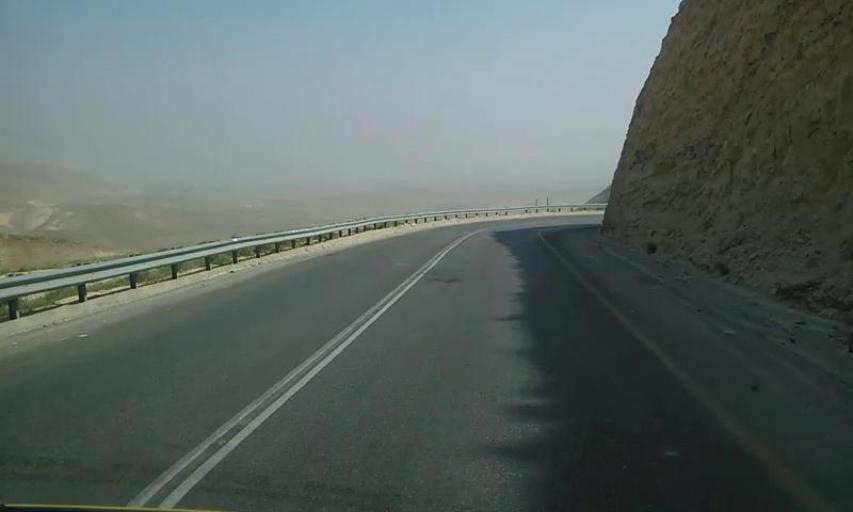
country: PS
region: West Bank
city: An Nuway`imah
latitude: 31.9120
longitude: 35.3794
